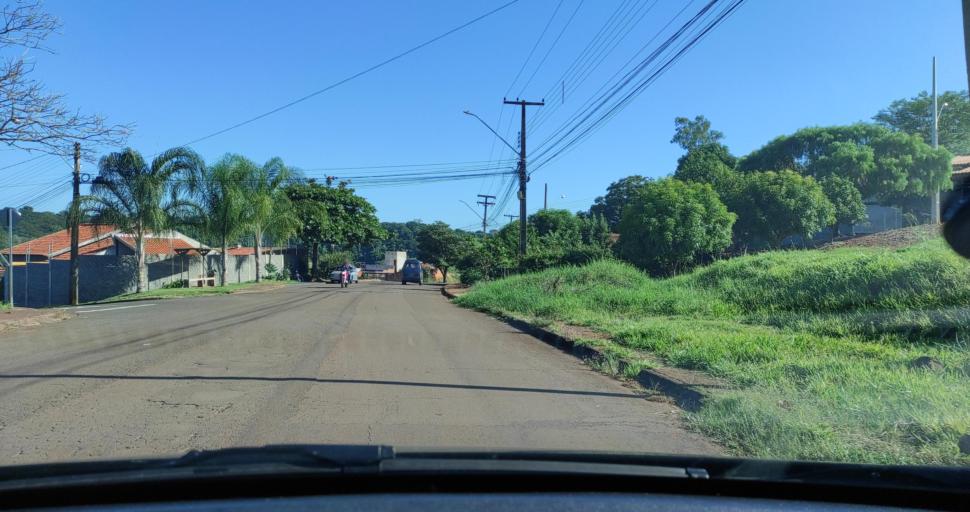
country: BR
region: Parana
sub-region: Ibipora
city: Ibipora
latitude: -23.2600
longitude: -51.0625
